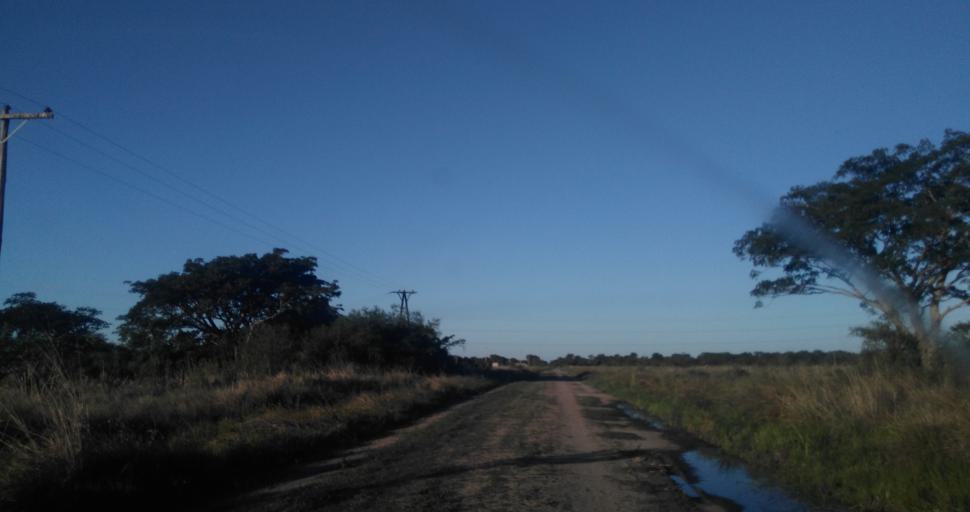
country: AR
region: Chaco
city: Fontana
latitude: -27.3905
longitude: -58.9780
